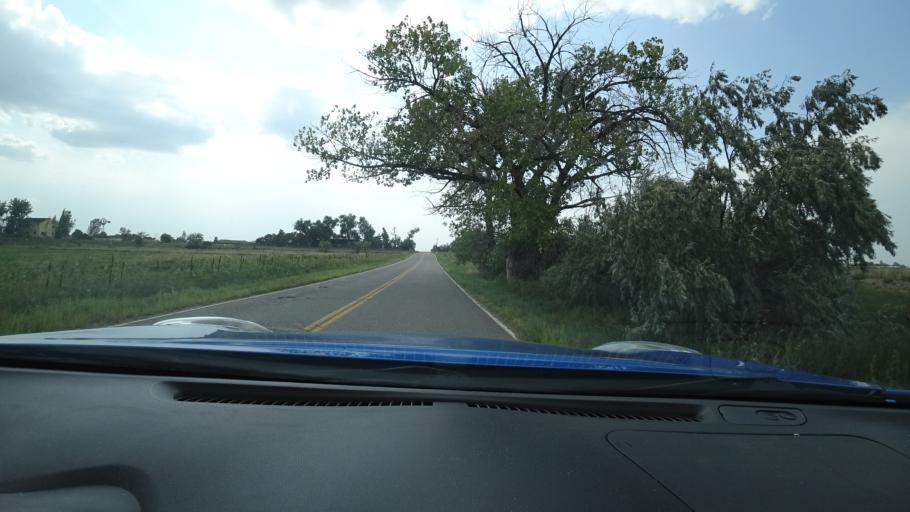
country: US
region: Colorado
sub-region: Adams County
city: Brighton
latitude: 39.9216
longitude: -104.8283
